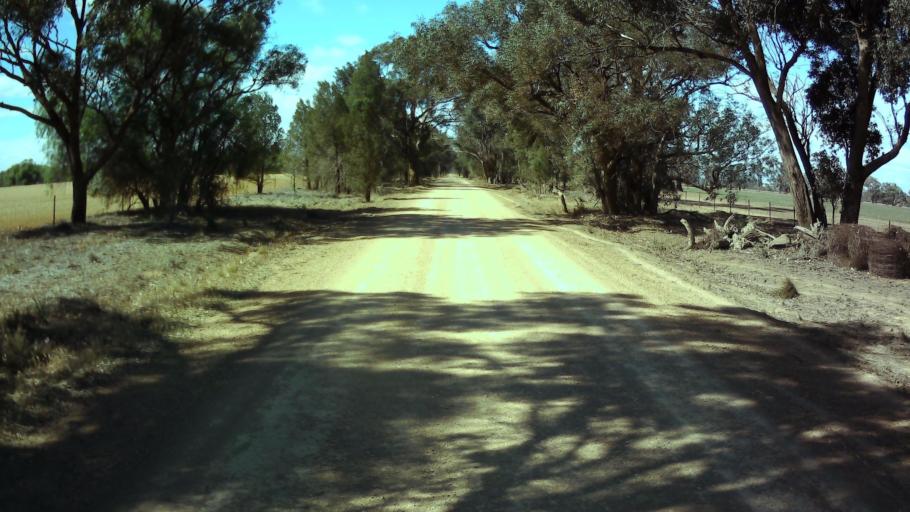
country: AU
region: New South Wales
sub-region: Weddin
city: Grenfell
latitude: -34.0401
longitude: 148.3159
